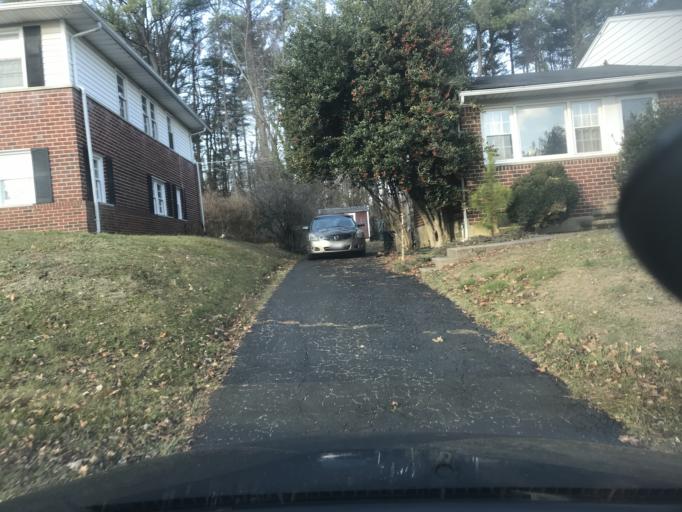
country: US
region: Maryland
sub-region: Baltimore County
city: Hampton
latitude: 39.4072
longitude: -76.5850
